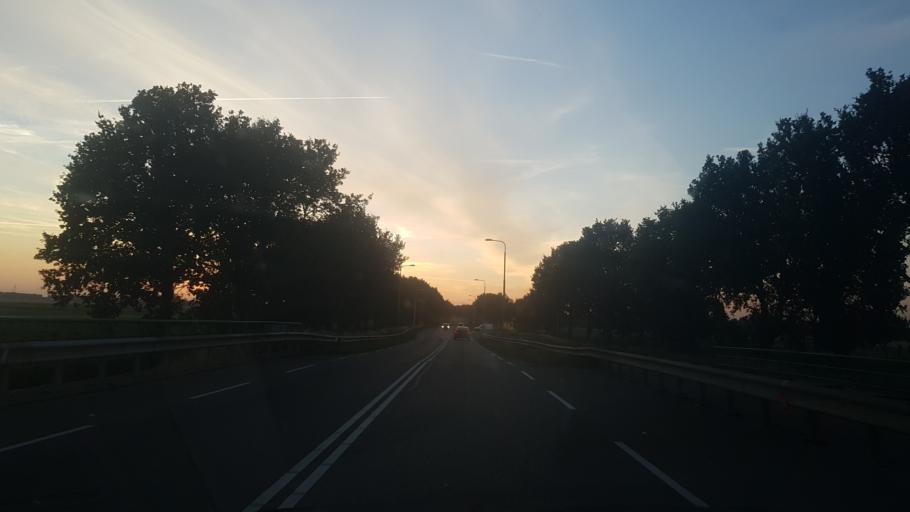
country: NL
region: Flevoland
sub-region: Gemeente Noordoostpolder
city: Emmeloord
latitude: 52.6965
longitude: 5.7268
